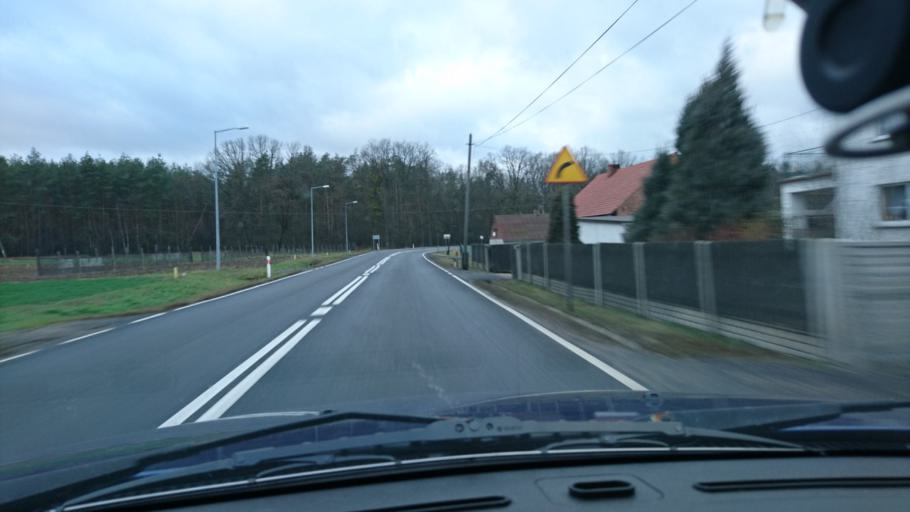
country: PL
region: Opole Voivodeship
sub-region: Powiat kluczborski
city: Kluczbork
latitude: 50.9471
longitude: 18.3168
